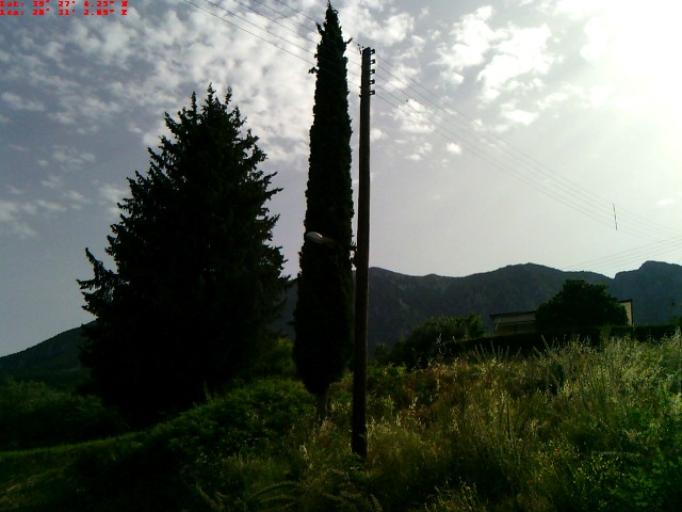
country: GR
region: Epirus
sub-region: Nomos Thesprotias
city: Paramythia
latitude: 39.4512
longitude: 20.5172
